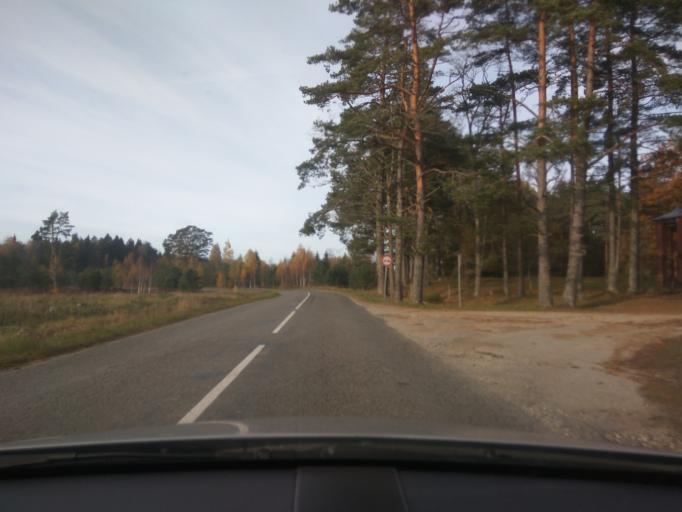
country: LV
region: Alsunga
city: Alsunga
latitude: 56.9884
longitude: 21.5155
